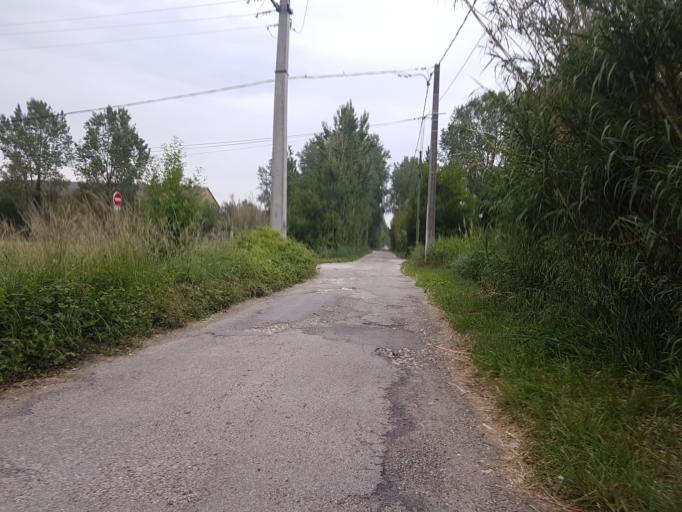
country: FR
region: Languedoc-Roussillon
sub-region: Departement du Gard
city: Roquemaure
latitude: 44.0647
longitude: 4.7780
